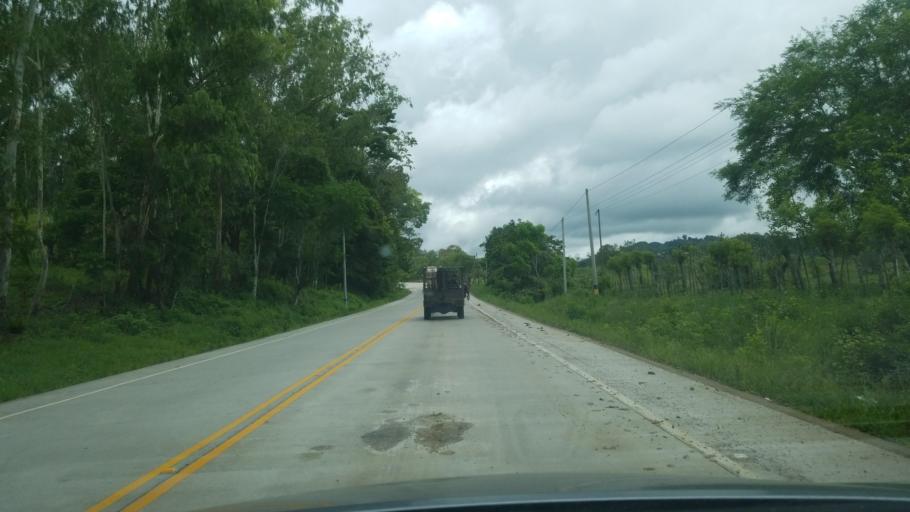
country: HN
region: Copan
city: San Jeronimo
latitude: 14.9803
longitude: -88.8803
